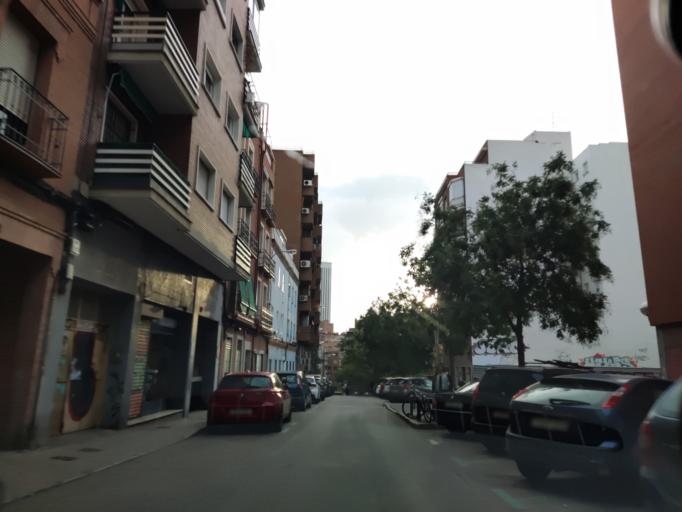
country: ES
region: Madrid
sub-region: Provincia de Madrid
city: Chamberi
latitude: 40.4513
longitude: -3.7008
